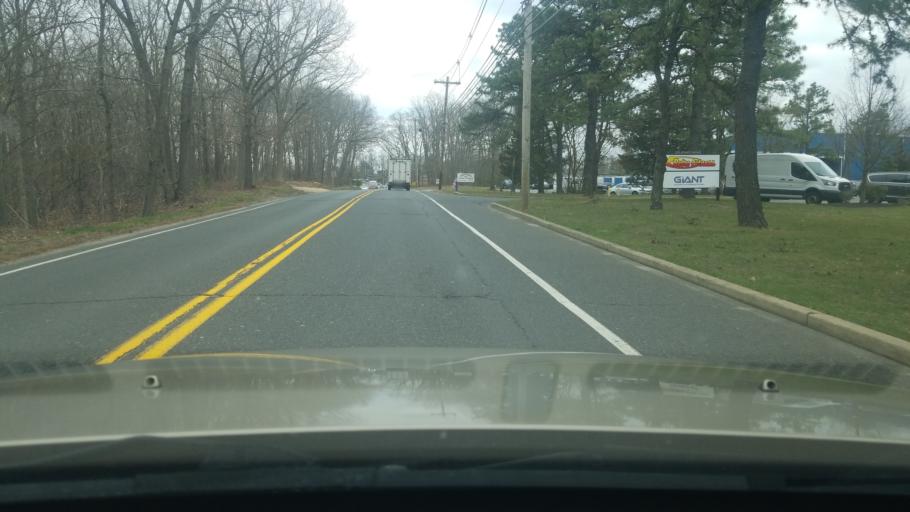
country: US
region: New Jersey
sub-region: Monmouth County
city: Manasquan
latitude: 40.1370
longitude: -74.0819
